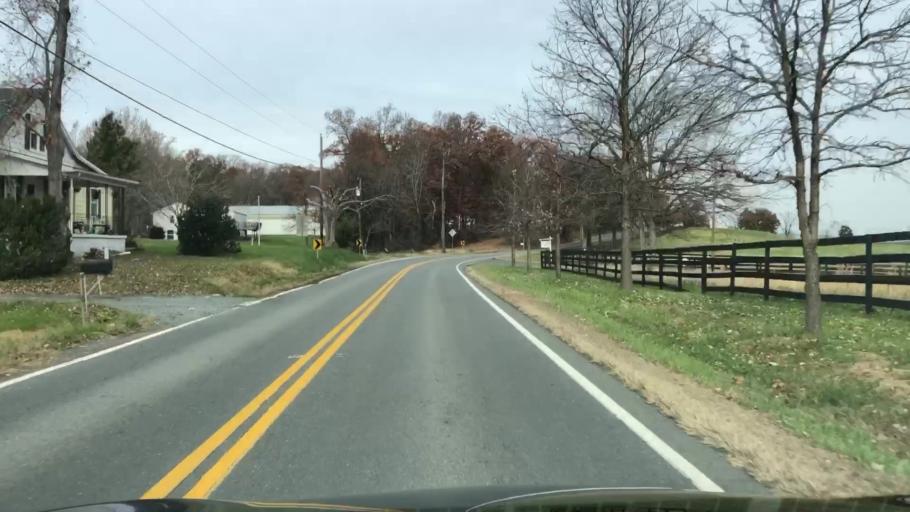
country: US
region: Virginia
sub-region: Fauquier County
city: New Baltimore
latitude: 38.7632
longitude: -77.6802
